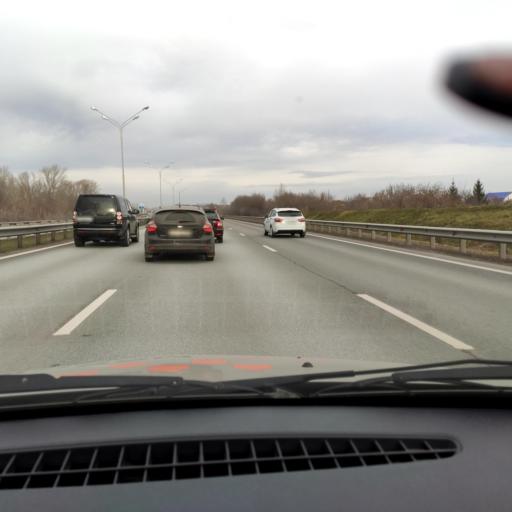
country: RU
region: Bashkortostan
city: Ufa
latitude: 54.6093
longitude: 55.9232
